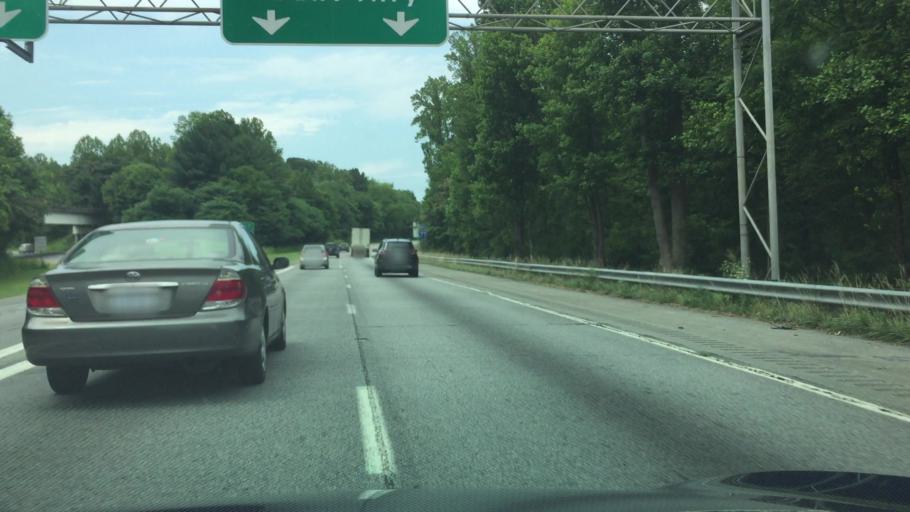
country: US
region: North Carolina
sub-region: Surry County
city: Elkin
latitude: 36.2631
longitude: -80.8246
